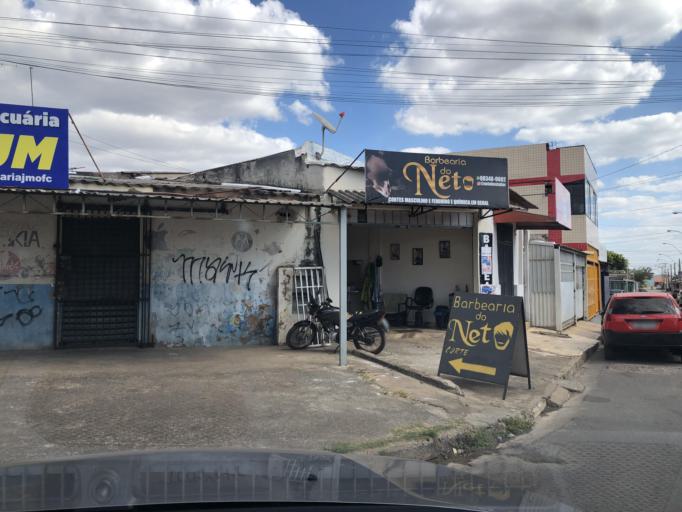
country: BR
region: Federal District
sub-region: Brasilia
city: Brasilia
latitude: -15.8939
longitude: -48.1424
